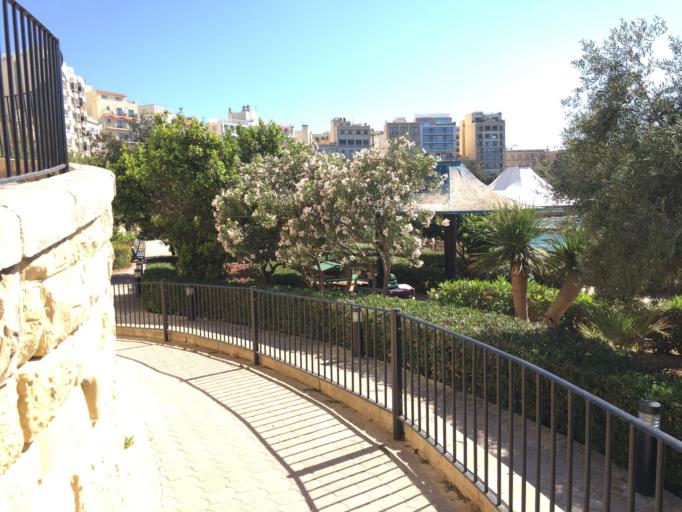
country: MT
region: Tas-Sliema
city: Sliema
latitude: 35.9162
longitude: 14.4982
